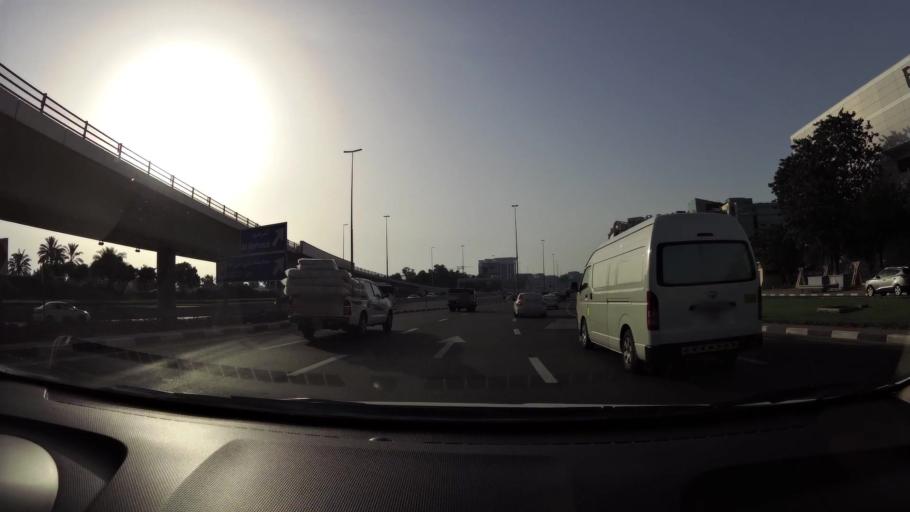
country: AE
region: Ash Shariqah
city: Sharjah
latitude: 25.2406
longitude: 55.3406
